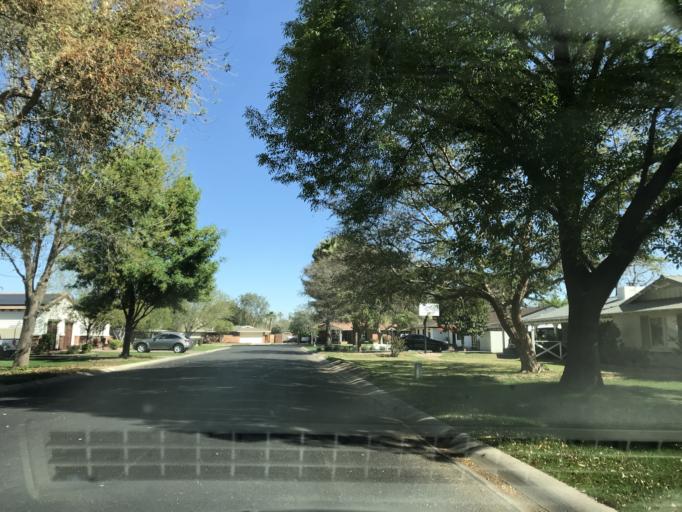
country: US
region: Arizona
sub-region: Maricopa County
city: Phoenix
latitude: 33.5189
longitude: -112.0775
